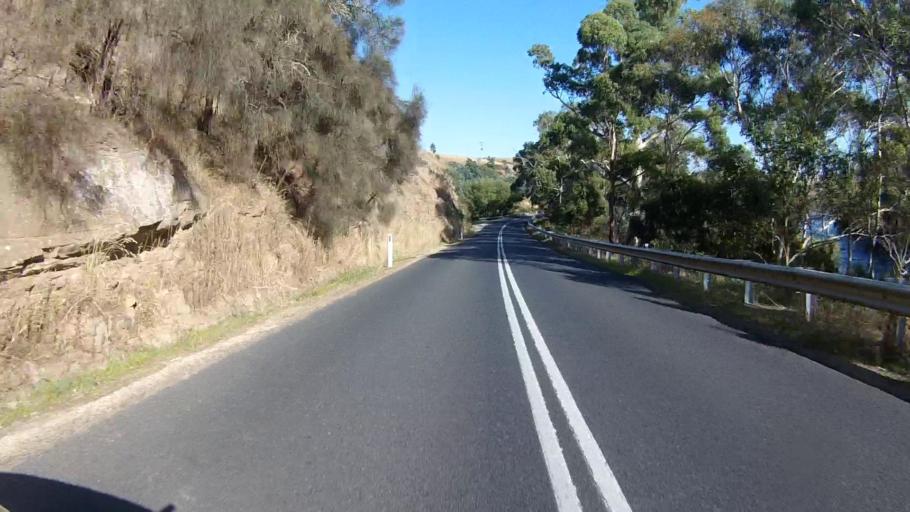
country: AU
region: Tasmania
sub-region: Derwent Valley
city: New Norfolk
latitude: -42.7590
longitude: 146.9896
